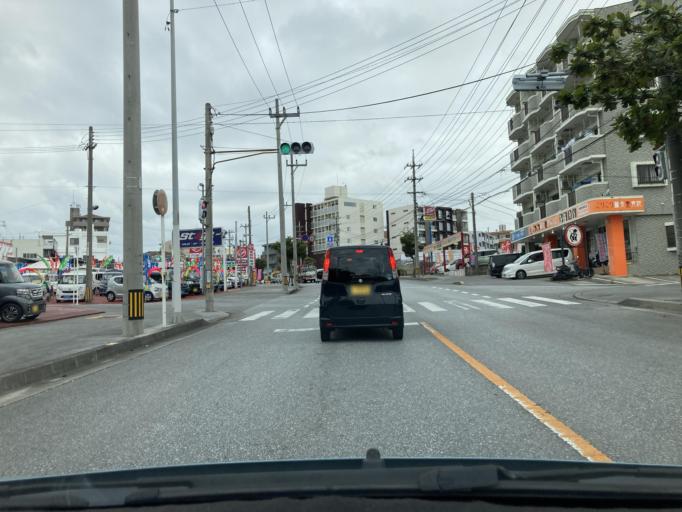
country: JP
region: Okinawa
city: Ginowan
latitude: 26.2436
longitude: 127.7644
